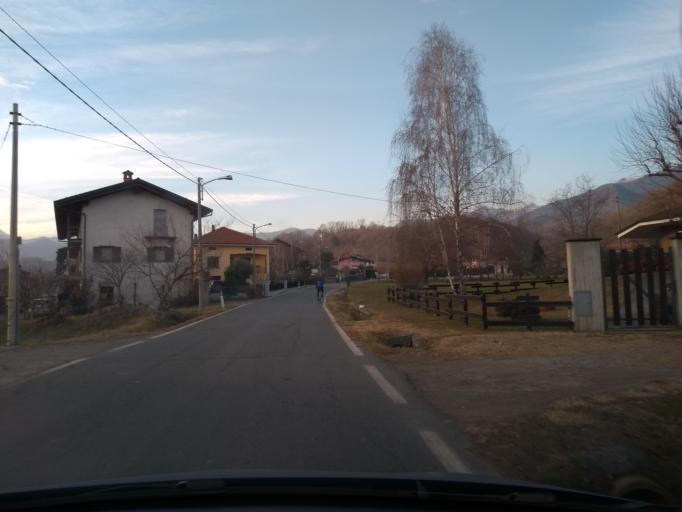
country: IT
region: Piedmont
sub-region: Provincia di Torino
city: Balangero
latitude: 45.2749
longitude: 7.5153
